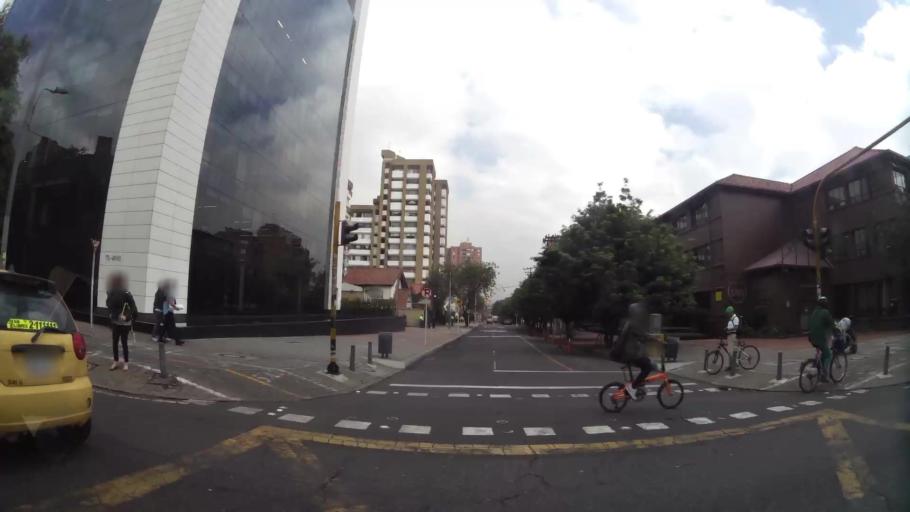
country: CO
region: Bogota D.C.
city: Barrio San Luis
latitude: 4.6627
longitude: -74.0549
